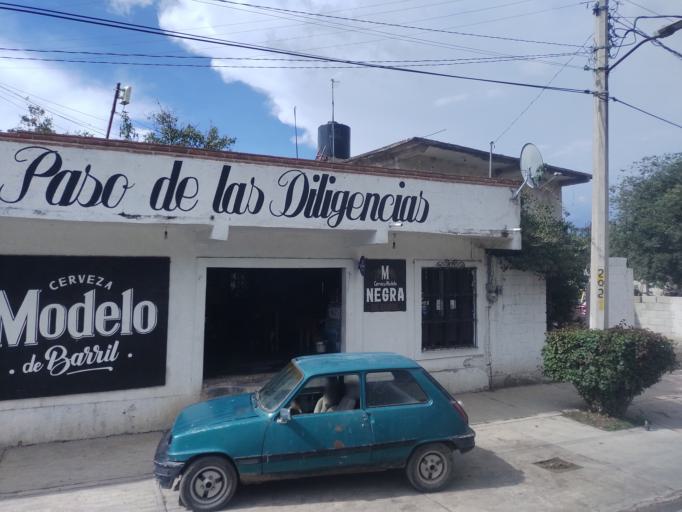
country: MX
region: Mexico
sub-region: Aculco
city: El Colorado
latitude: 20.1044
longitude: -99.7327
